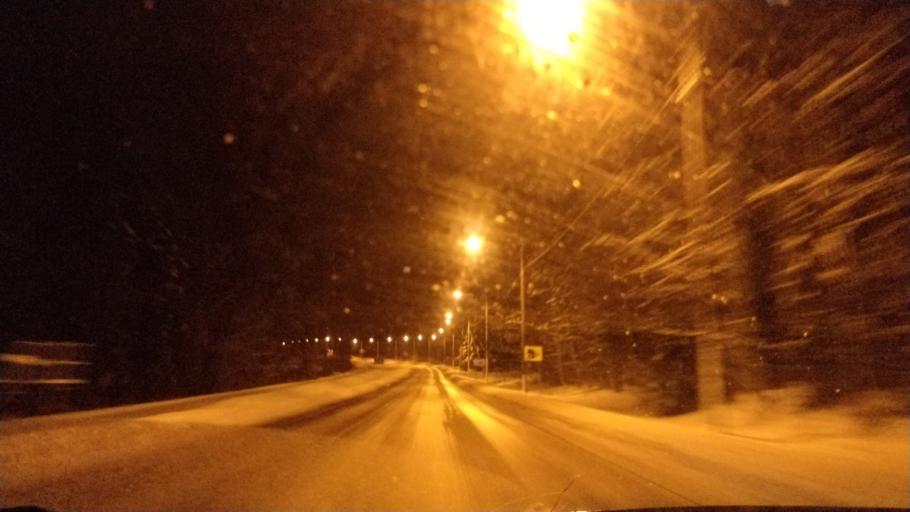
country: FI
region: Lapland
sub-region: Rovaniemi
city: Rovaniemi
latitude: 66.2699
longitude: 25.3312
